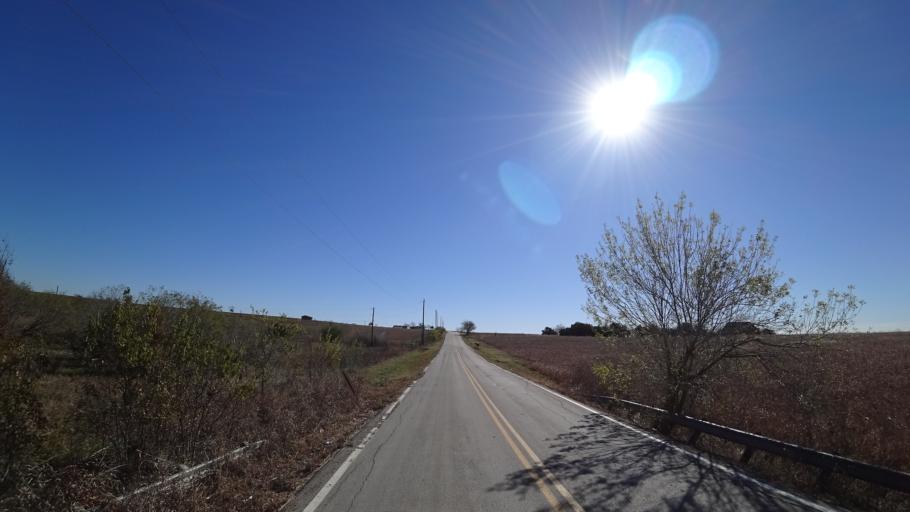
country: US
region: Texas
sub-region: Travis County
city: Garfield
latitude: 30.1077
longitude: -97.6468
